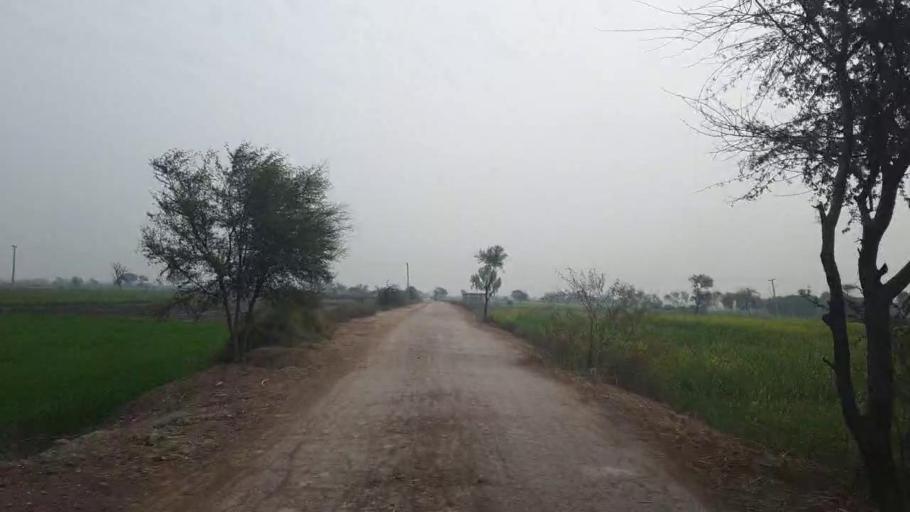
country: PK
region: Sindh
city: Tando Adam
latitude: 25.7243
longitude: 68.7330
